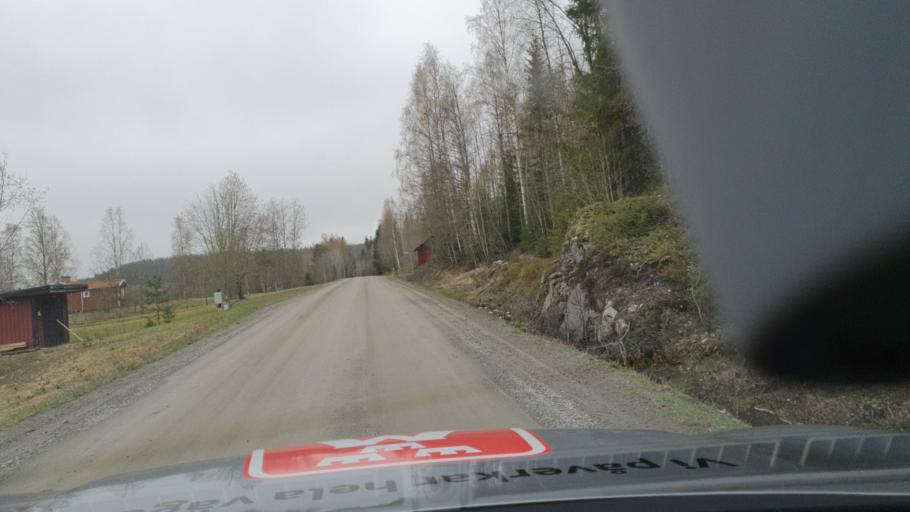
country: SE
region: Vaesternorrland
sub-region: OErnskoeldsviks Kommun
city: Husum
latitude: 63.6388
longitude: 19.0588
